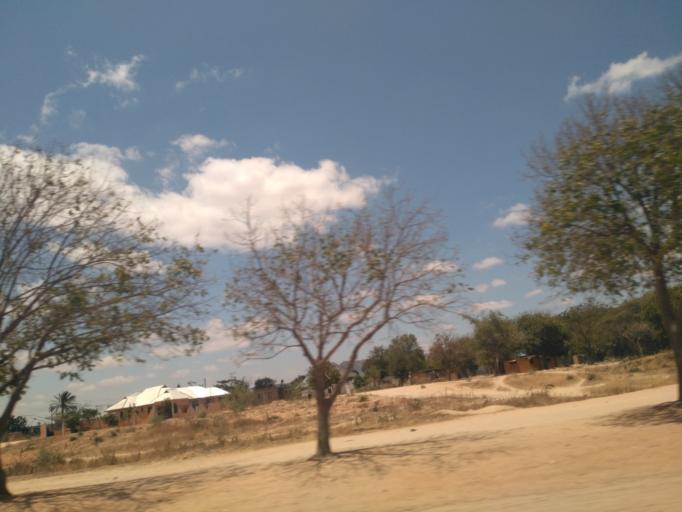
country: TZ
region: Dodoma
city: Kisasa
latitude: -6.1719
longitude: 35.7699
